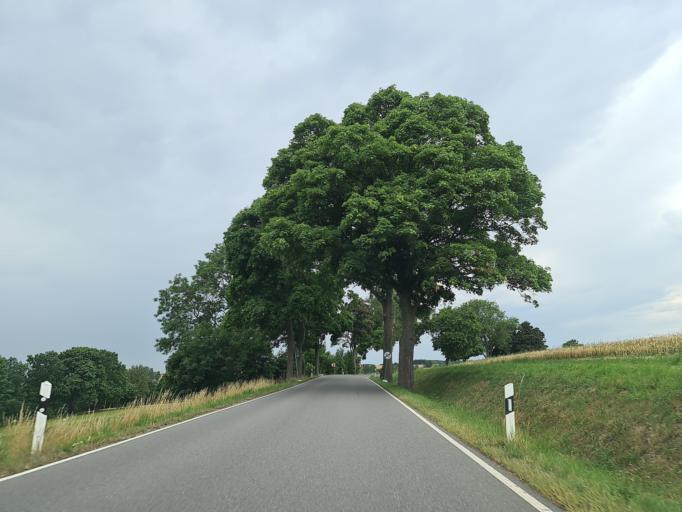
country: DE
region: Saxony
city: Pfaffroda
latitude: 50.7289
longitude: 13.3366
